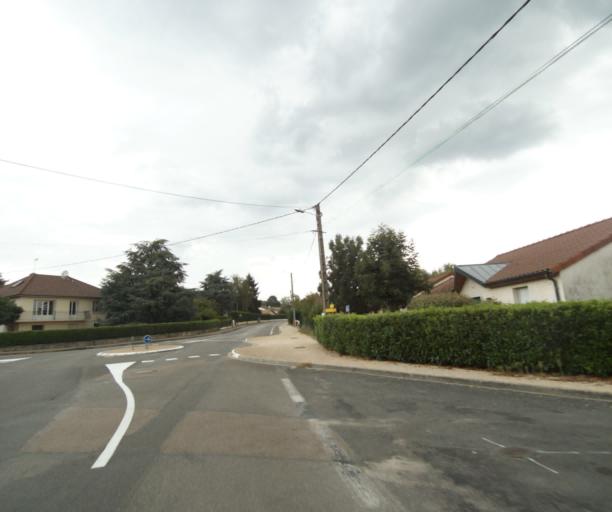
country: FR
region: Bourgogne
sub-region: Departement de Saone-et-Loire
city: Tournus
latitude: 46.5707
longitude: 4.9008
